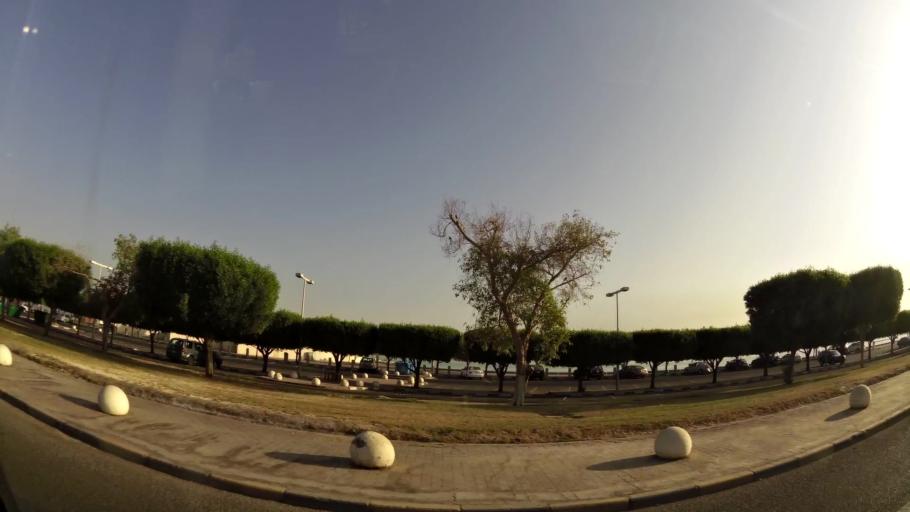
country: KW
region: Muhafazat Hawalli
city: Hawalli
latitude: 29.3464
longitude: 48.0406
